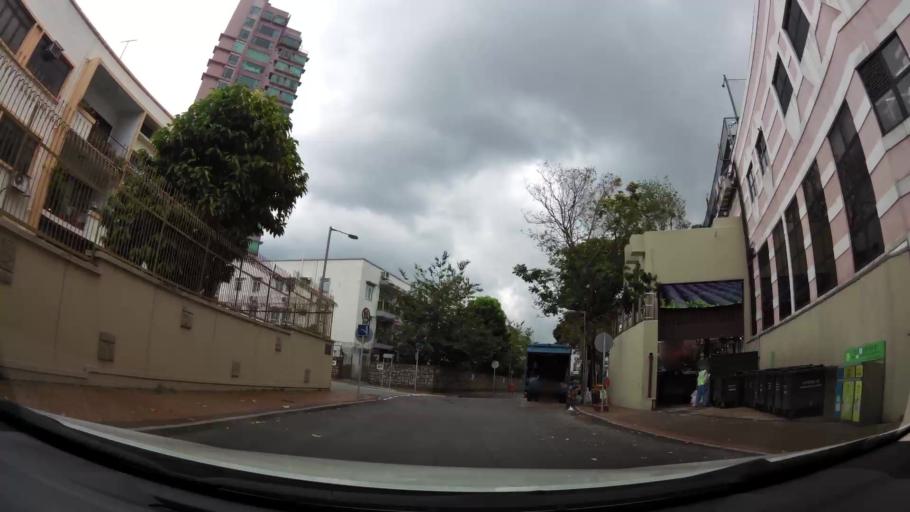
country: HK
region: Sham Shui Po
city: Sham Shui Po
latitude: 22.3321
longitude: 114.1728
